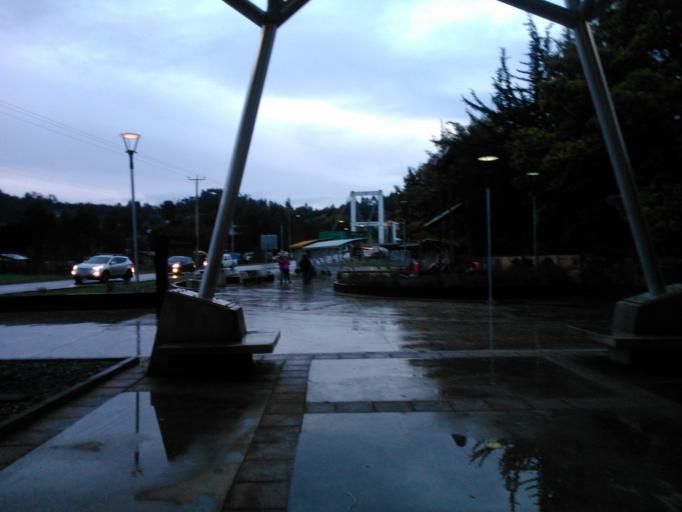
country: CL
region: Araucania
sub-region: Provincia de Cautin
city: Carahue
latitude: -38.7185
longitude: -73.1725
